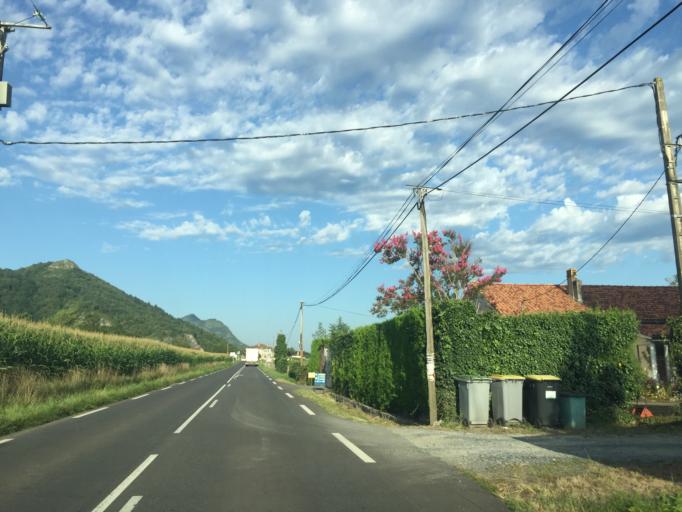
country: FR
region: Midi-Pyrenees
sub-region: Departement des Hautes-Pyrenees
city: Lourdes
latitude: 43.0947
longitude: -0.0113
